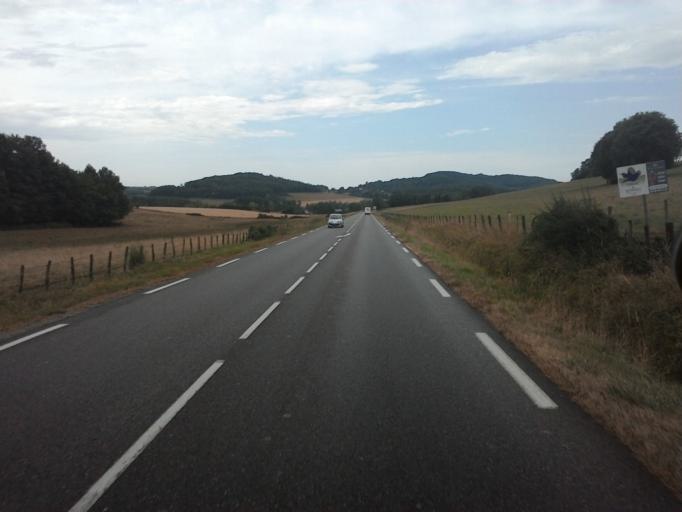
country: FR
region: Franche-Comte
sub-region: Departement du Jura
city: Poligny
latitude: 46.8219
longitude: 5.5944
